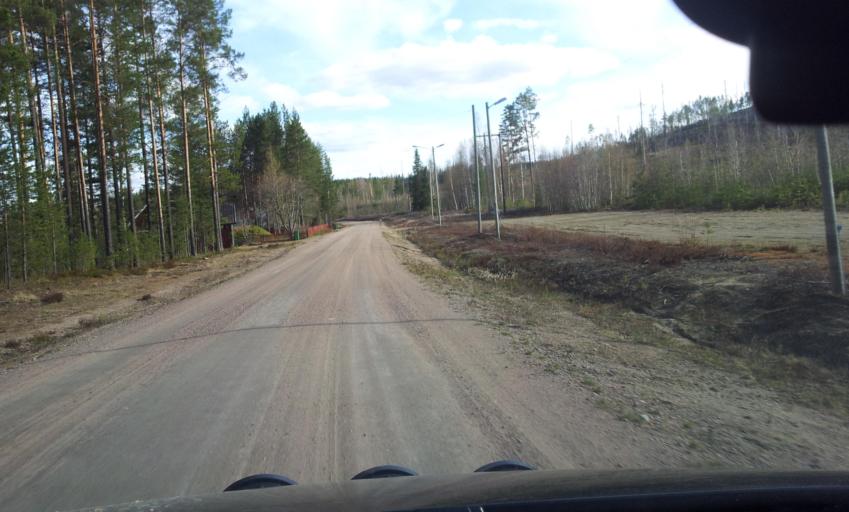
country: SE
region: Vaesternorrland
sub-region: Ange Kommun
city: Ange
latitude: 62.1653
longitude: 15.6587
